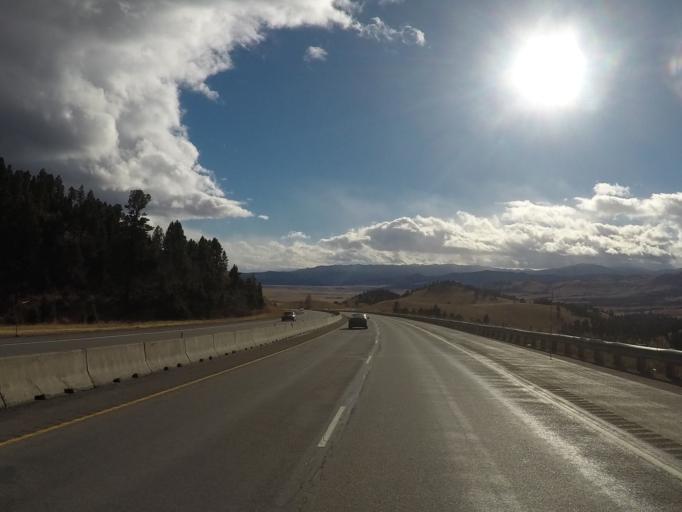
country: US
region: Montana
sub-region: Jefferson County
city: Boulder
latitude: 46.3171
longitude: -112.0765
